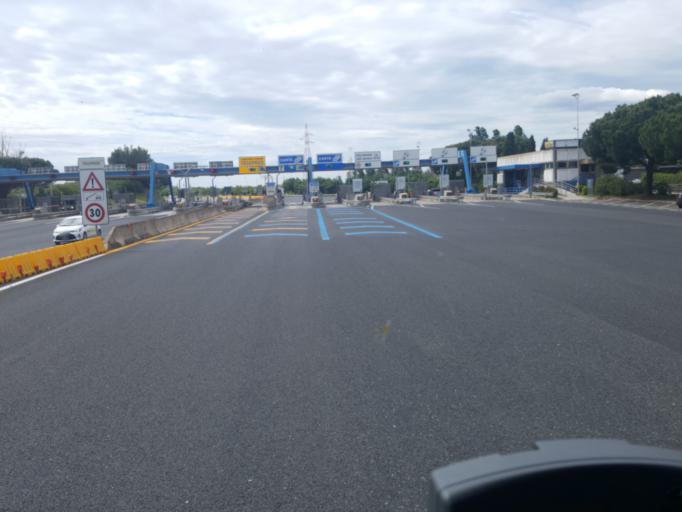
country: IT
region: Latium
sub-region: Citta metropolitana di Roma Capitale
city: Ara Nova
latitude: 41.9155
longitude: 12.2121
